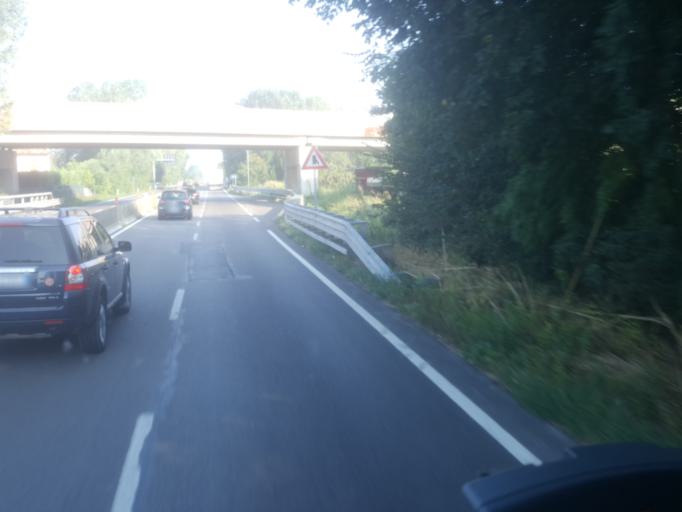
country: IT
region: Emilia-Romagna
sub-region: Provincia di Ravenna
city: Ravenna
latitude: 44.3990
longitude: 12.1810
